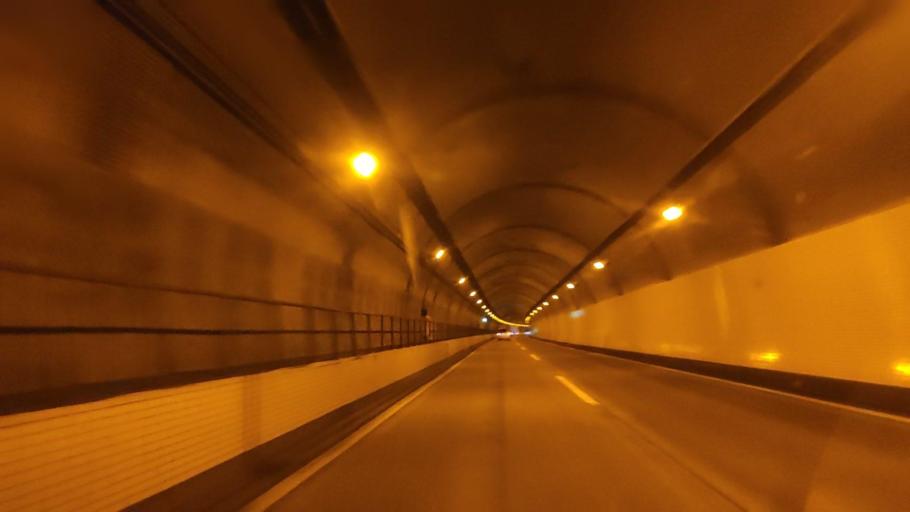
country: JP
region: Niigata
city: Joetsu
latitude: 37.1356
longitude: 138.0604
